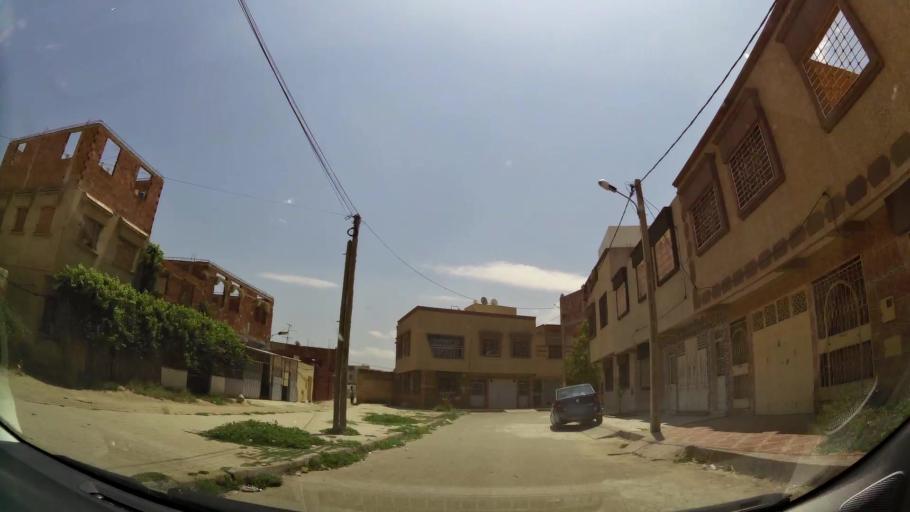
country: MA
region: Oriental
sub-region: Oujda-Angad
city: Oujda
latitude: 34.6847
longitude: -1.8977
